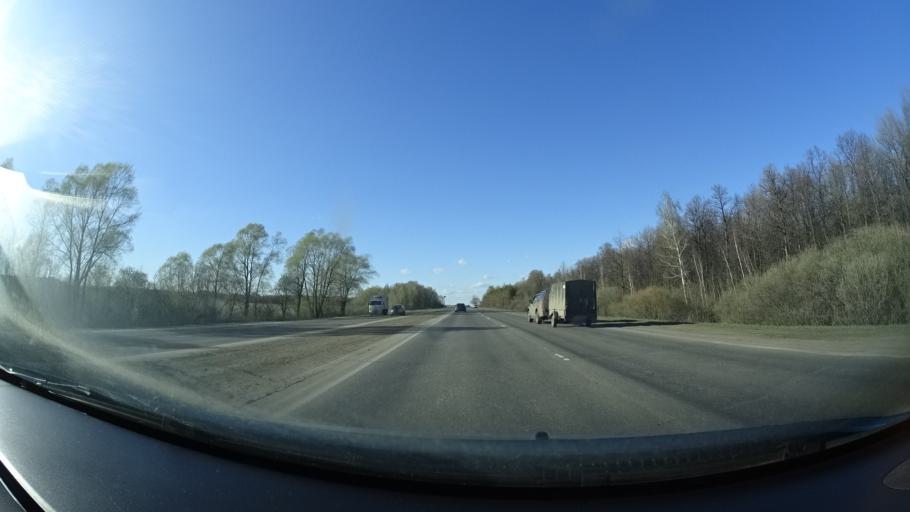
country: RU
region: Bashkortostan
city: Kabakovo
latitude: 54.4528
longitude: 55.9180
